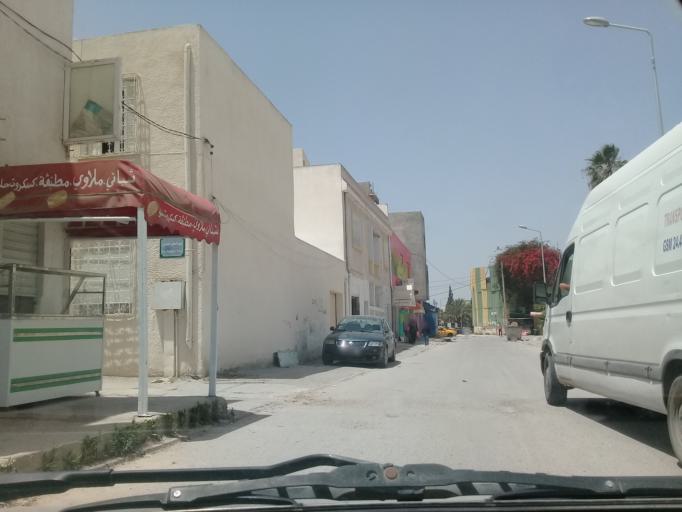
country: TN
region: Ariana
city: Ariana
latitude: 36.8319
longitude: 10.1967
